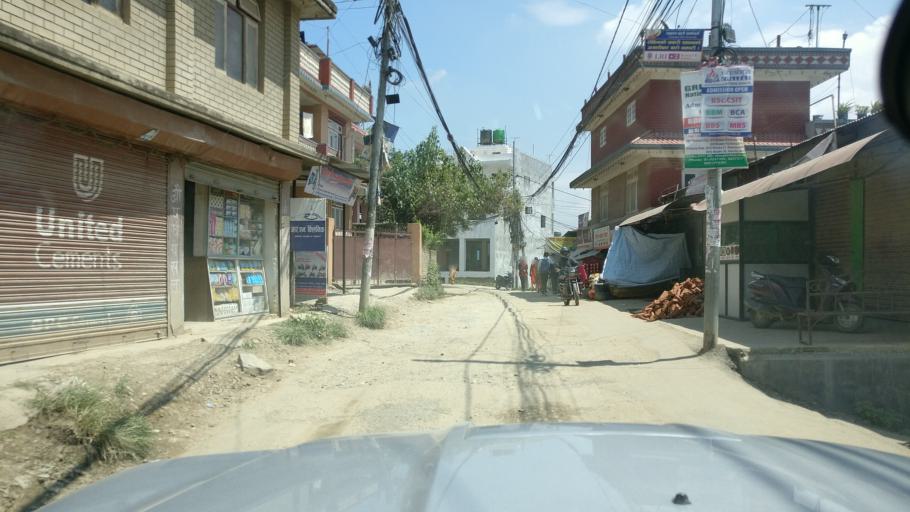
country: NP
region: Central Region
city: Kirtipur
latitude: 27.6939
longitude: 85.2753
